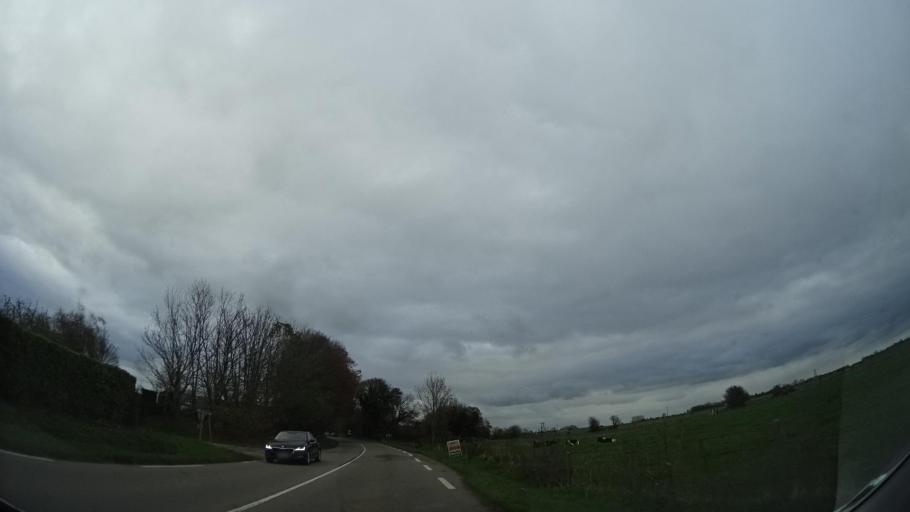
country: FR
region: Haute-Normandie
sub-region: Departement de la Seine-Maritime
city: Cauville-sur-Mer
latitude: 49.5794
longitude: 0.1233
